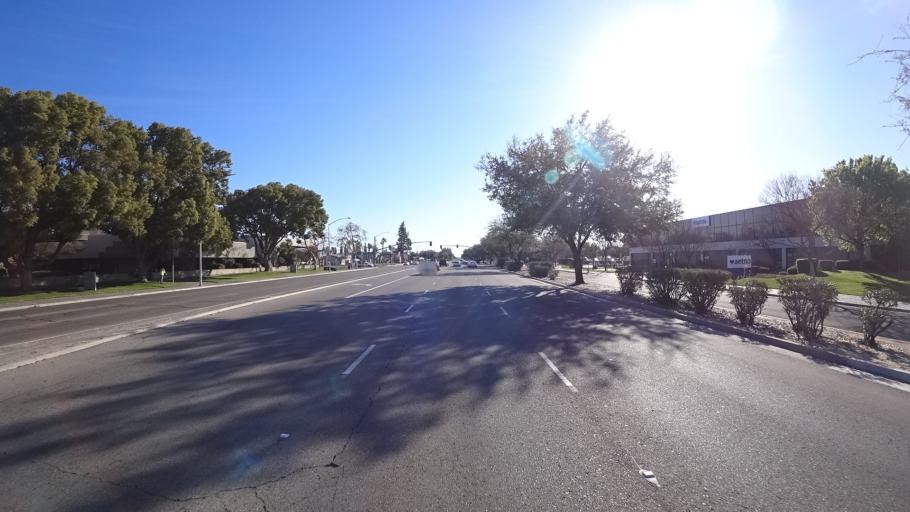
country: US
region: California
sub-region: Fresno County
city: Fresno
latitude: 36.8085
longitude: -119.7647
